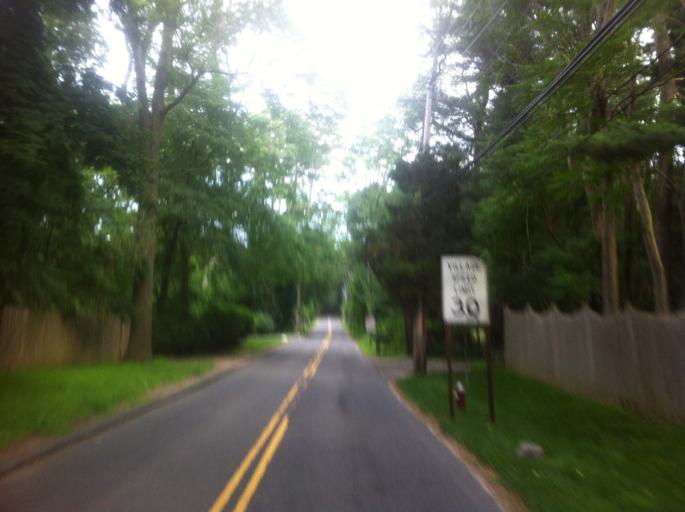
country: US
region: New York
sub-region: Nassau County
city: Bayville
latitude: 40.8946
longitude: -73.5747
